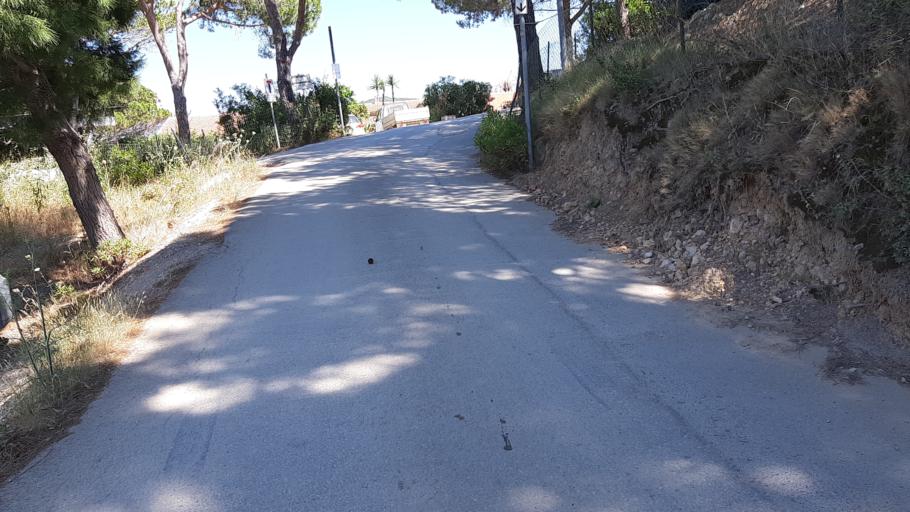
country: IT
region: Tuscany
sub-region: Provincia di Livorno
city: Portoferraio
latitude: 42.7596
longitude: 10.2982
